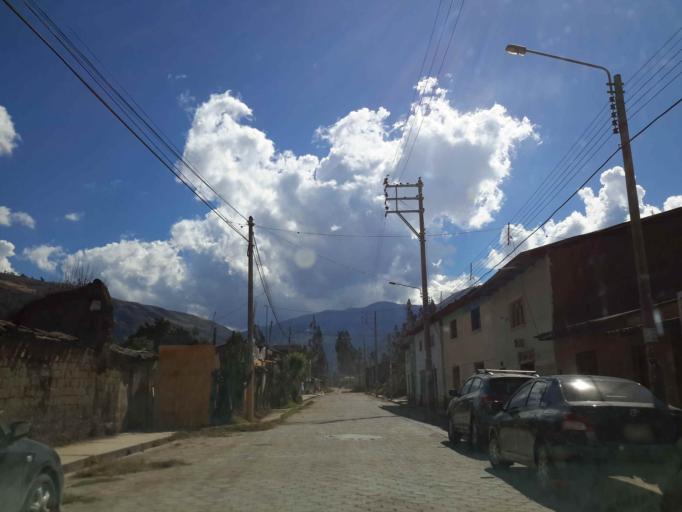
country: PE
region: Apurimac
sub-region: Provincia de Andahuaylas
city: Talavera
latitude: -13.6510
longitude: -73.4354
